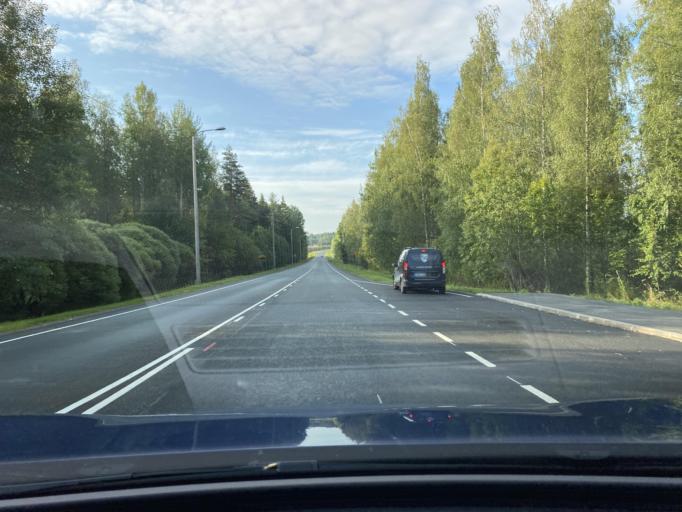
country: FI
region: Kymenlaakso
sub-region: Kouvola
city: Kouvola
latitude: 60.8937
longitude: 26.6041
